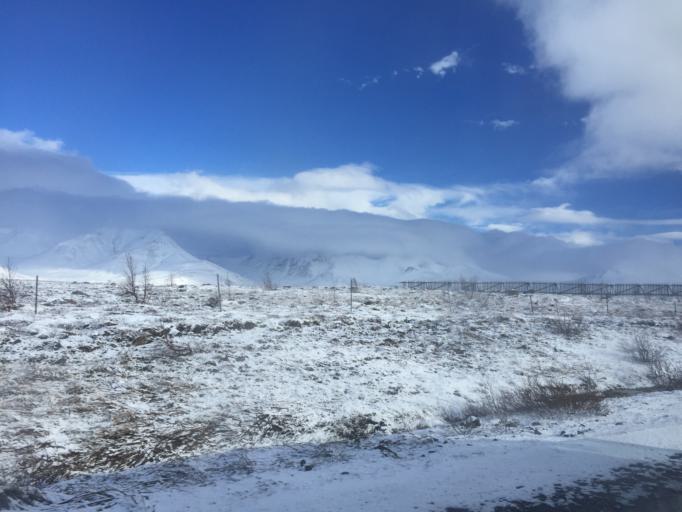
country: IS
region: Capital Region
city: Mosfellsbaer
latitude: 64.1818
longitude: -21.5804
